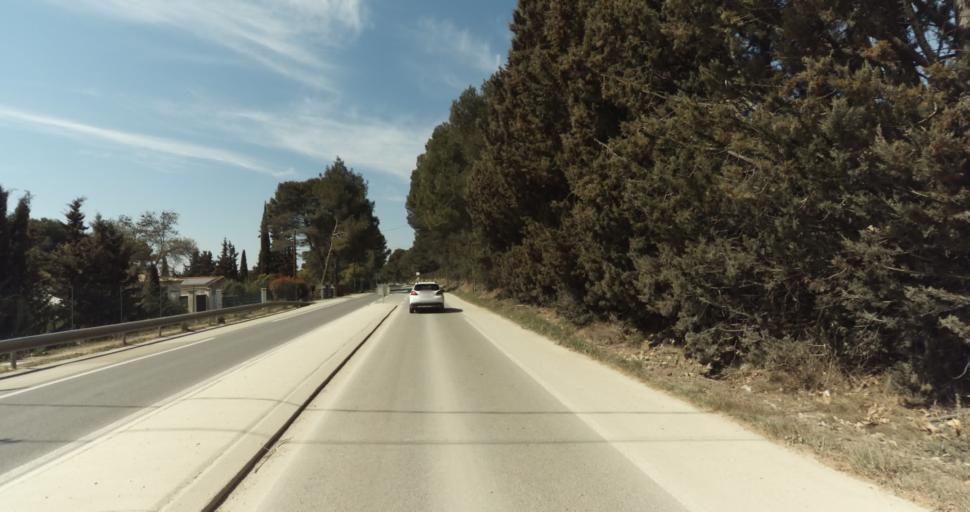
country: FR
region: Provence-Alpes-Cote d'Azur
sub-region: Departement des Bouches-du-Rhone
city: Ventabren
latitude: 43.5481
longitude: 5.3087
